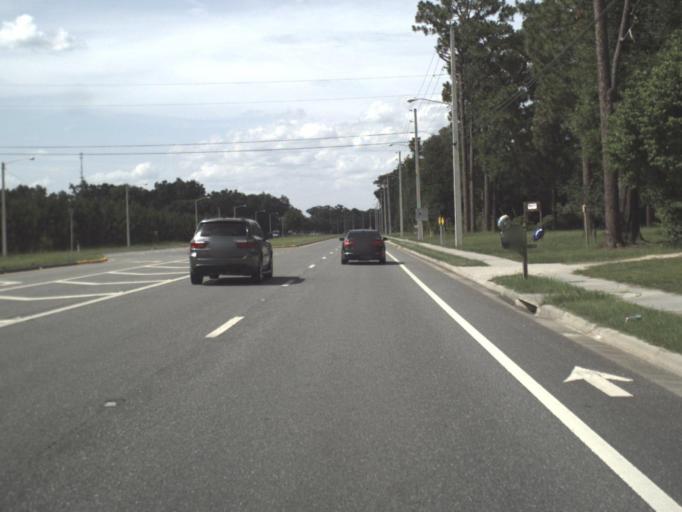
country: US
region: Florida
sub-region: Columbia County
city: Lake City
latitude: 30.1342
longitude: -82.6514
